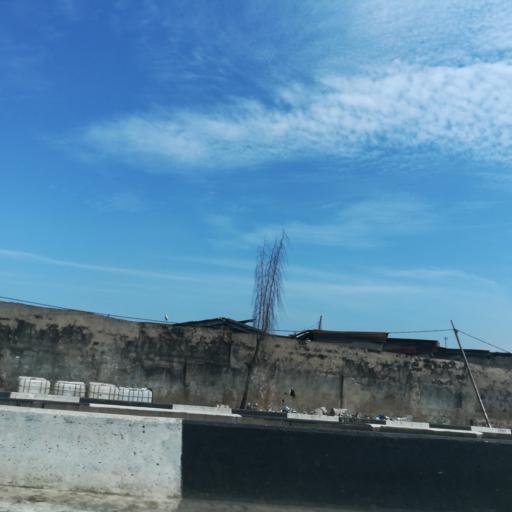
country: NG
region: Lagos
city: Lagos
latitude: 6.4598
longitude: 3.3943
